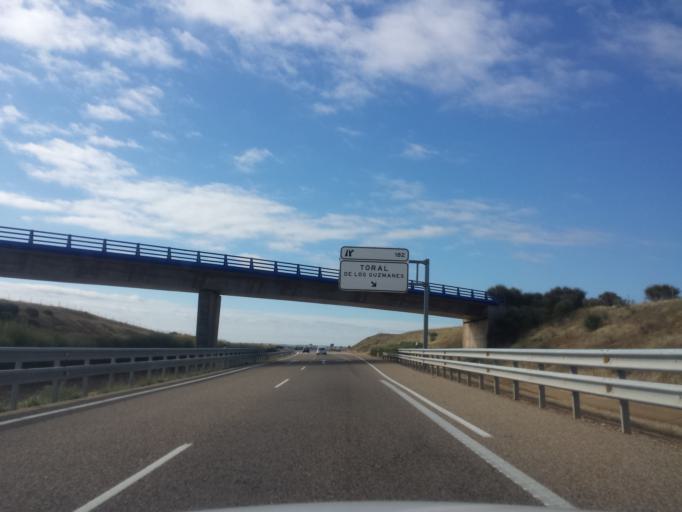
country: ES
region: Castille and Leon
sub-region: Provincia de Leon
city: Toral de los Guzmanes
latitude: 42.2519
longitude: -5.5941
